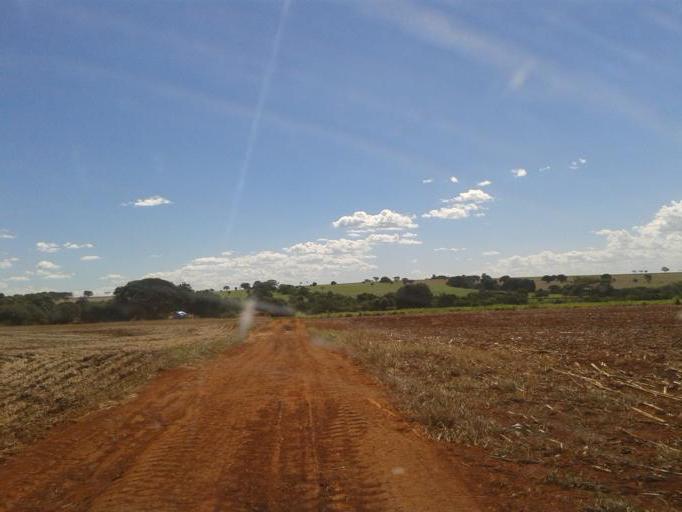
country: BR
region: Minas Gerais
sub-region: Capinopolis
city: Capinopolis
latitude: -18.6493
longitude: -49.5699
